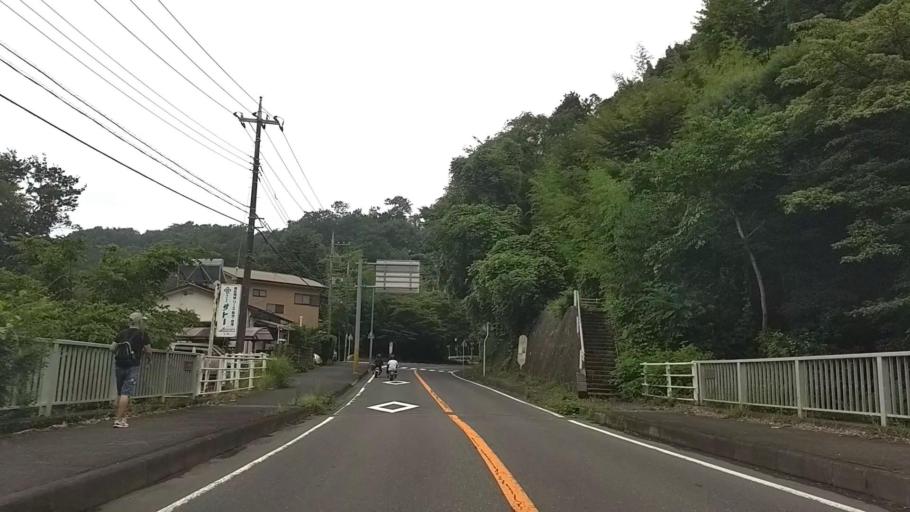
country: JP
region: Kanagawa
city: Hadano
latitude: 35.3377
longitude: 139.2224
